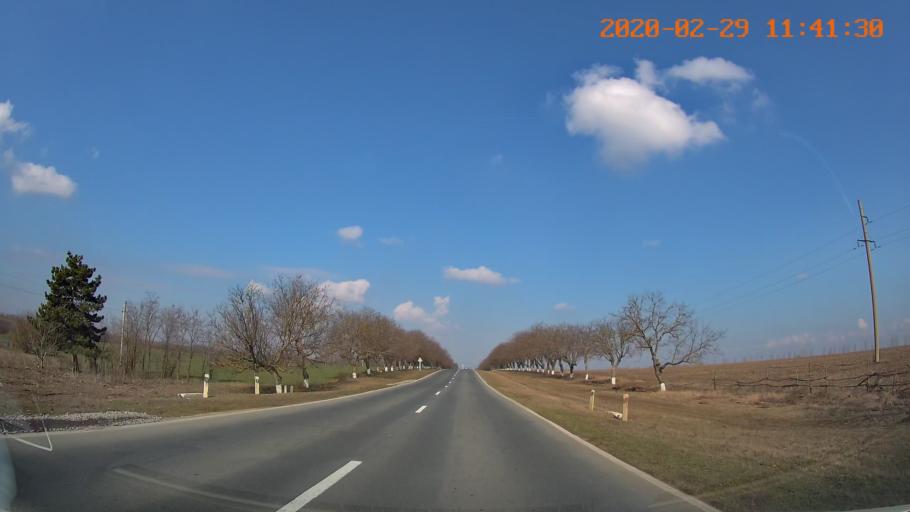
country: MD
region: Rezina
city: Saharna
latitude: 47.6722
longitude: 29.0163
